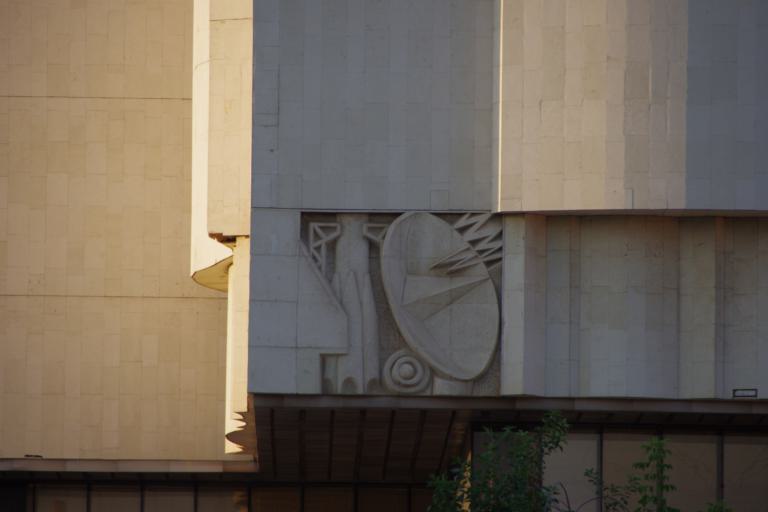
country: RU
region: Samara
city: Samara
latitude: 53.1917
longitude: 50.1079
